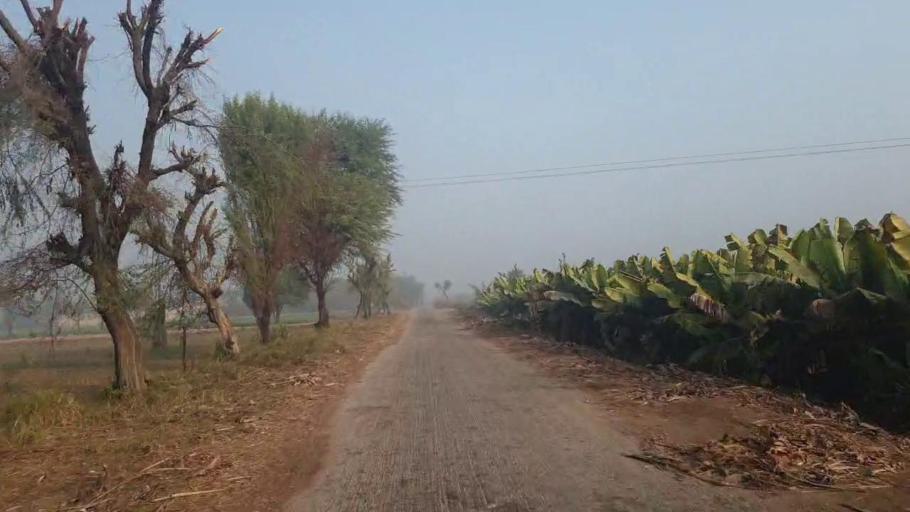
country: PK
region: Sindh
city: Tando Adam
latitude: 25.7874
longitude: 68.6334
